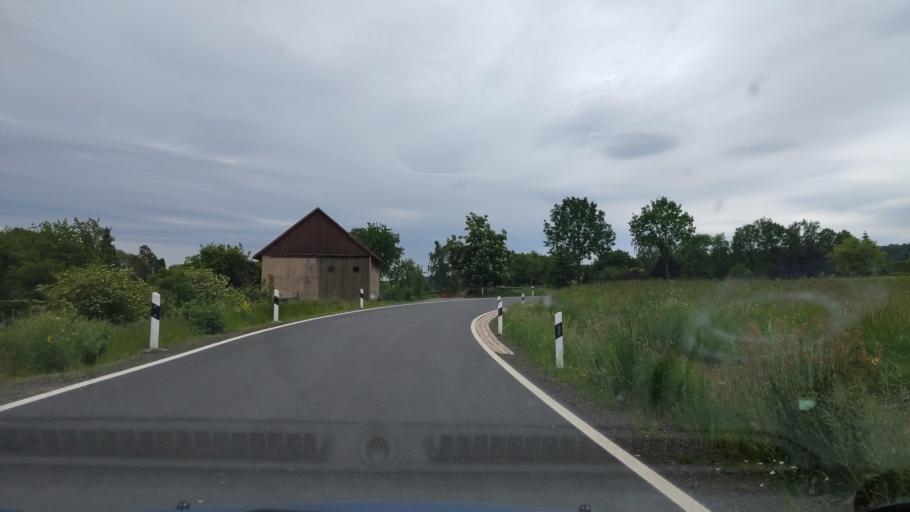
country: DE
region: Lower Saxony
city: Hardegsen
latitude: 51.7031
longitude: 9.7834
